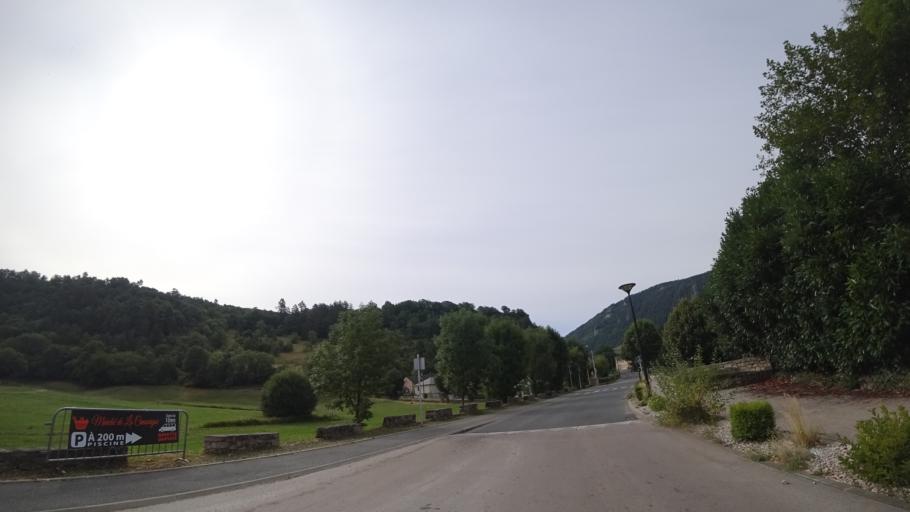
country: FR
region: Languedoc-Roussillon
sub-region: Departement de la Lozere
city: La Canourgue
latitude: 44.4286
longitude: 3.2221
